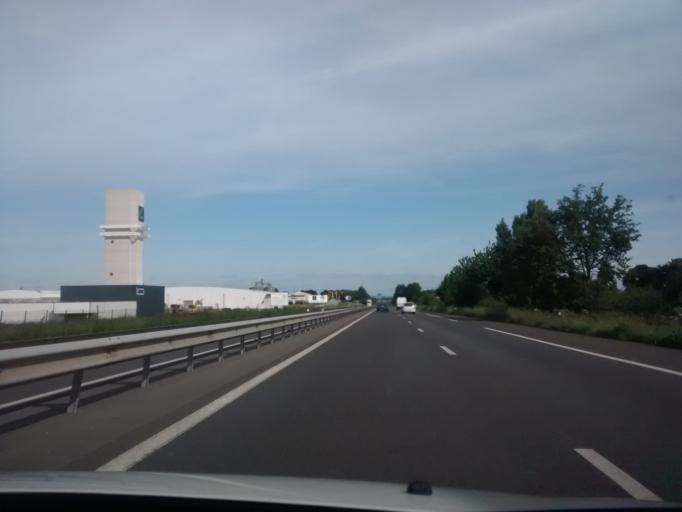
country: FR
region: Brittany
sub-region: Departement des Cotes-d'Armor
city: Broons
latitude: 48.3138
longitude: -2.2431
